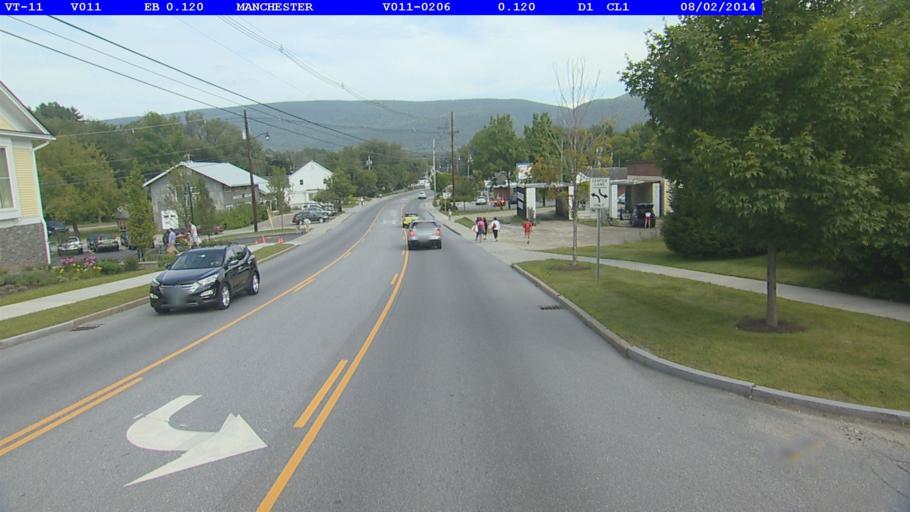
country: US
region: Vermont
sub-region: Bennington County
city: Manchester Center
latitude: 43.1755
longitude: -73.0553
